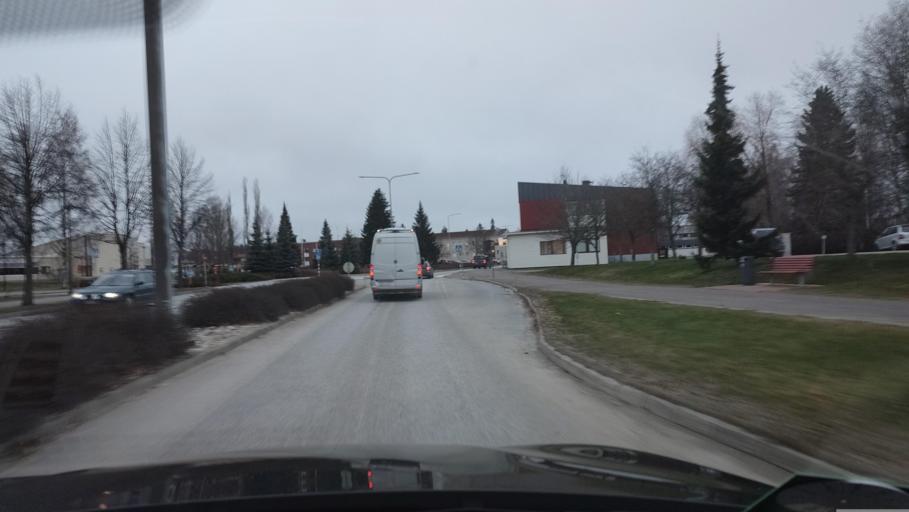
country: FI
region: Southern Ostrobothnia
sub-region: Suupohja
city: Kauhajoki
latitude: 62.4216
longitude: 22.1754
